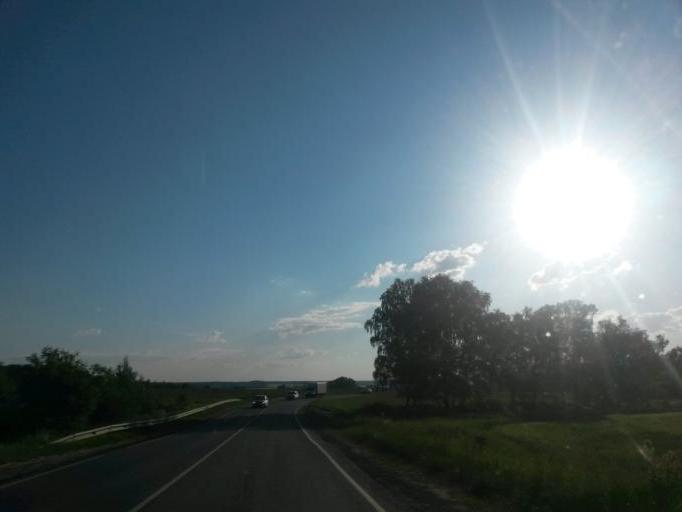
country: RU
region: Moskovskaya
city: Vostryakovo
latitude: 55.3525
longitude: 37.7546
